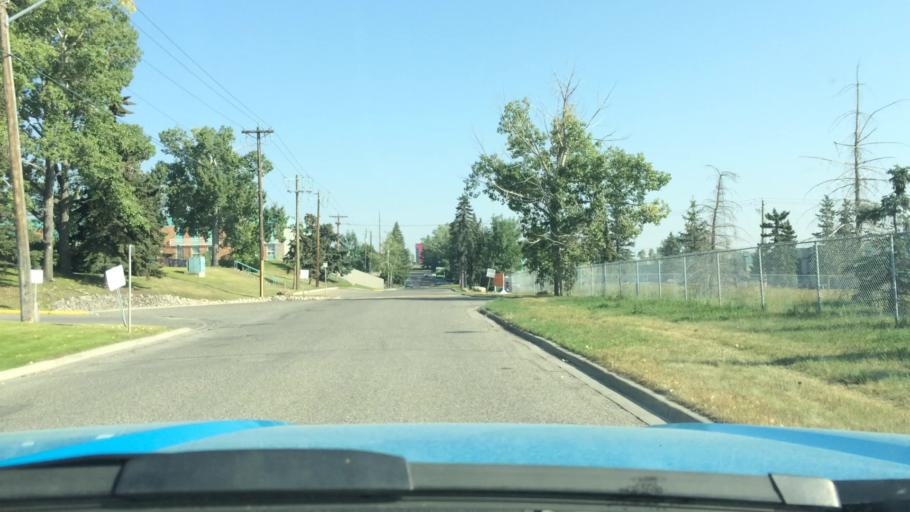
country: CA
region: Alberta
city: Calgary
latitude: 50.9907
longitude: -114.0484
